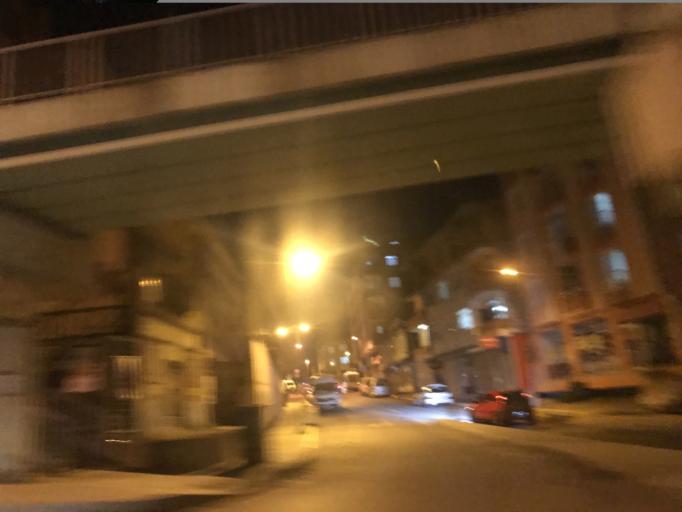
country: TR
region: Istanbul
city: Pendik
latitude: 40.8908
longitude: 29.2401
